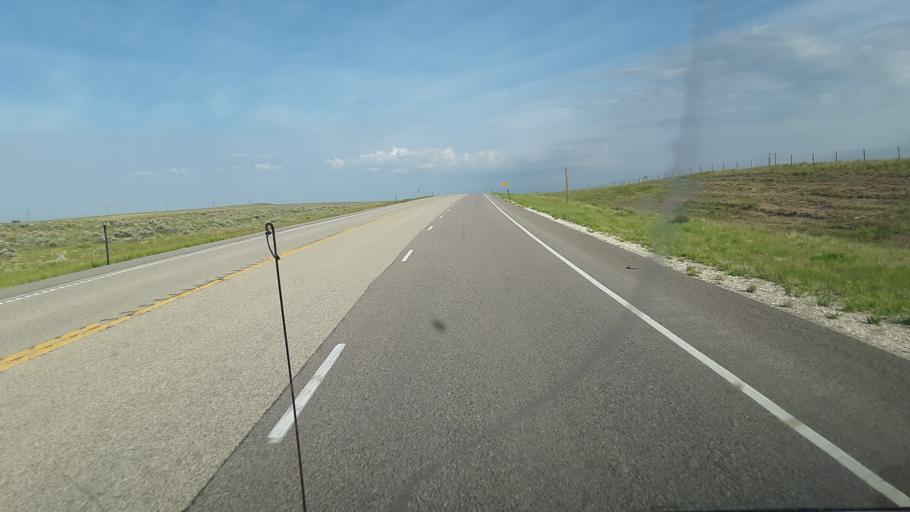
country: US
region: Wyoming
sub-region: Natrona County
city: Mills
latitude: 43.0417
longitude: -107.0737
